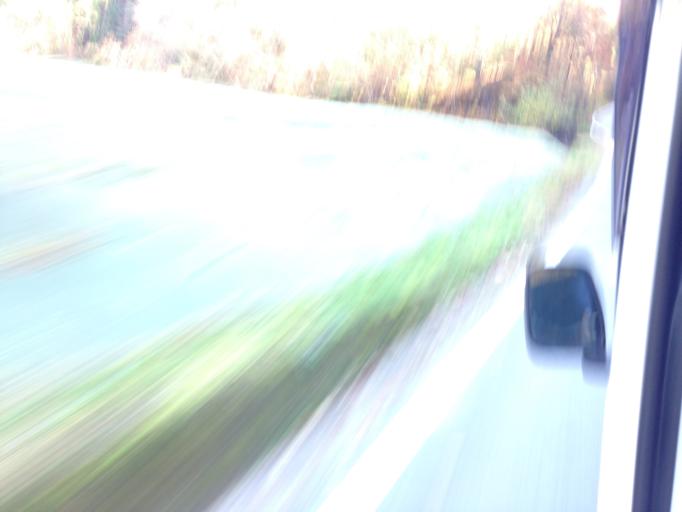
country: JP
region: Gifu
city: Mitake
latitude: 35.6053
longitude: 137.1962
